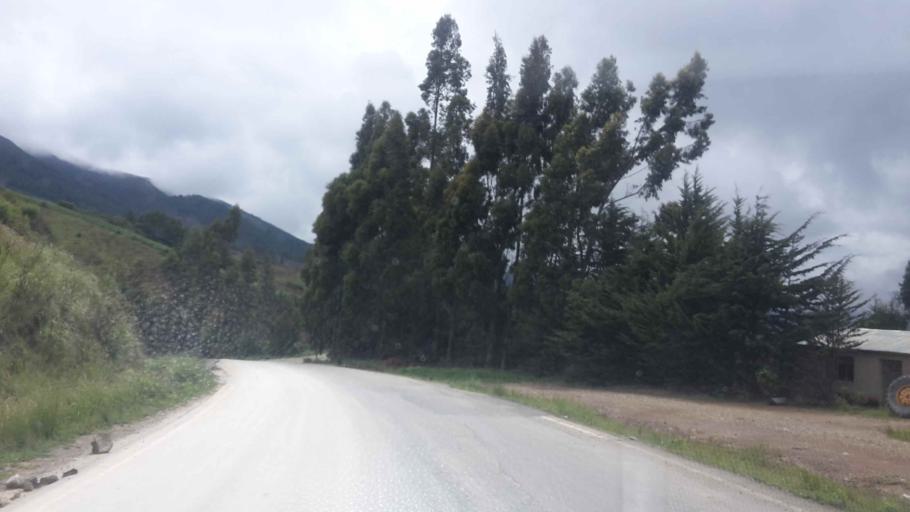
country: BO
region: Cochabamba
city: Totora
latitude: -17.5689
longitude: -65.3245
